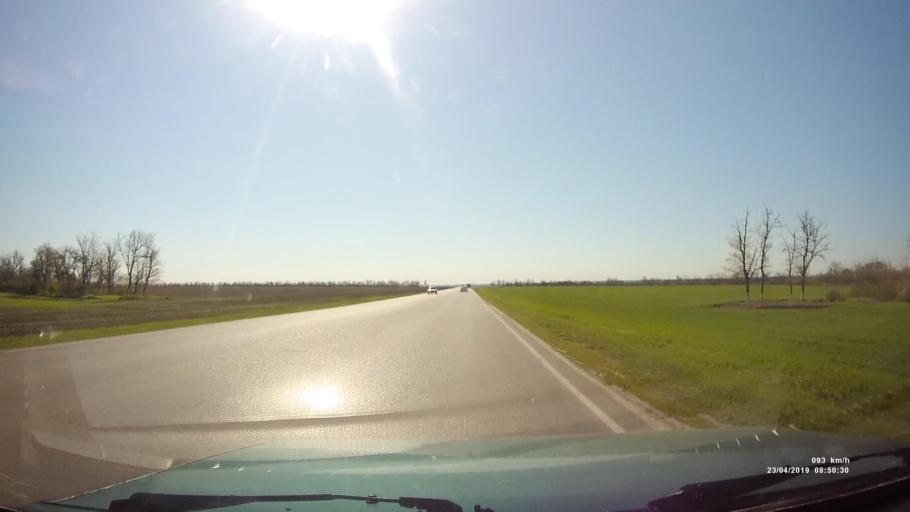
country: RU
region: Rostov
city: Gigant
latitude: 46.4961
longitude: 41.4283
